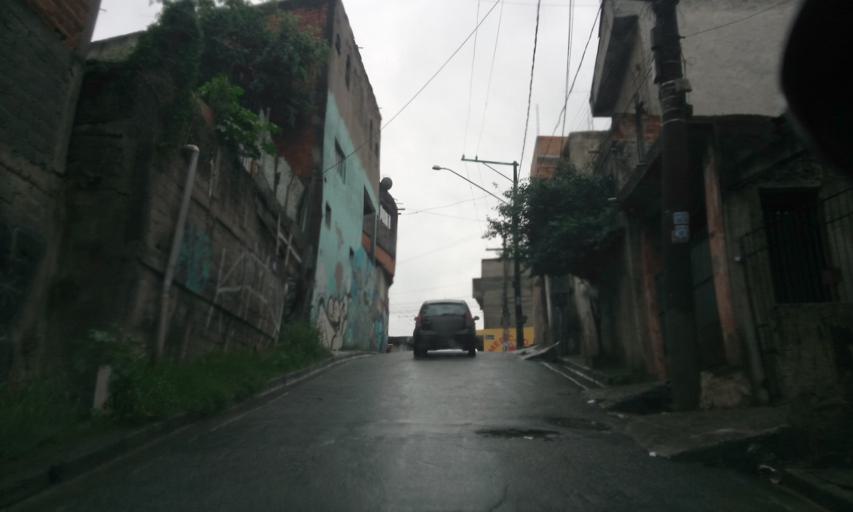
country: BR
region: Sao Paulo
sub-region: Santo Andre
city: Santo Andre
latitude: -23.7074
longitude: -46.5173
